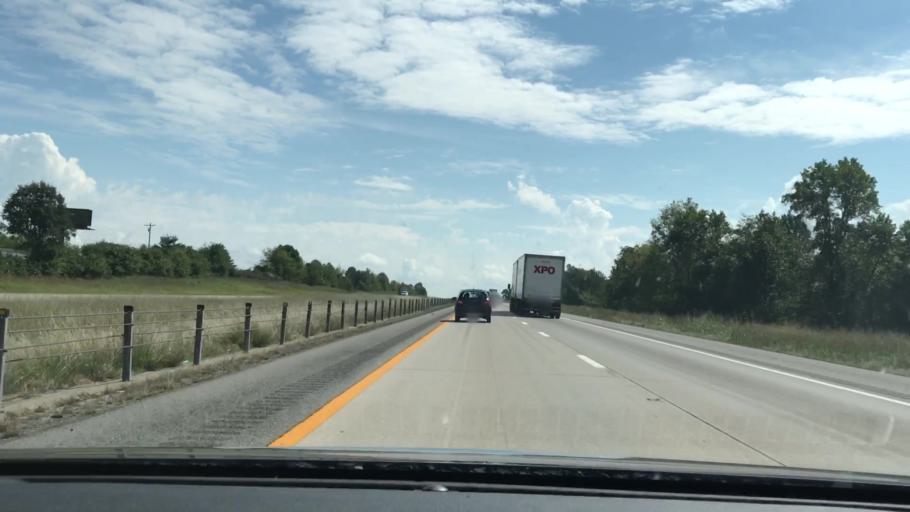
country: US
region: Kentucky
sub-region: Christian County
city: Oak Grove
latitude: 36.6723
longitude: -87.3895
